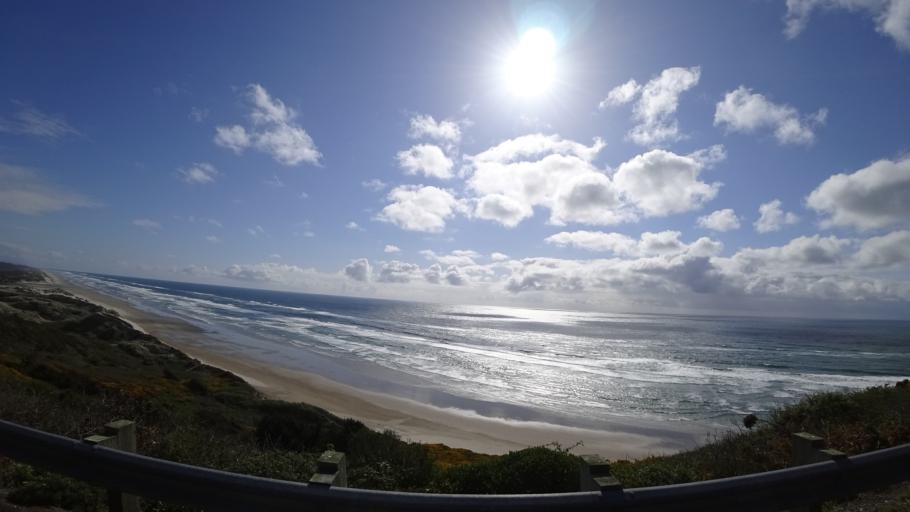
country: US
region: Oregon
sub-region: Lane County
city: Florence
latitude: 44.1036
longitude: -124.1211
